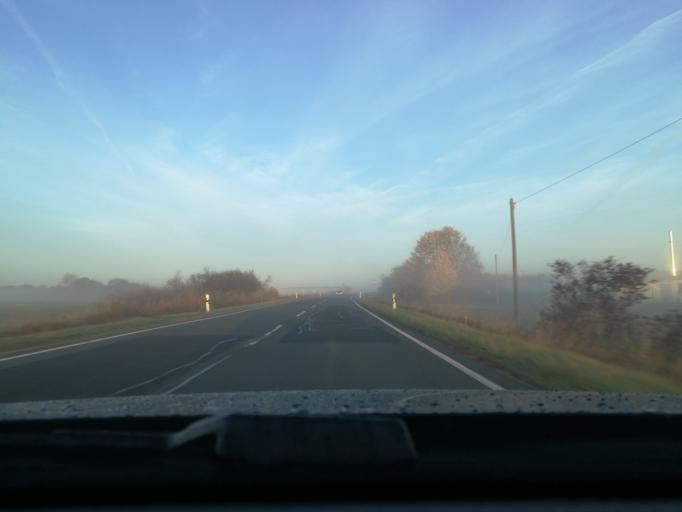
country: DE
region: Bavaria
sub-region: Regierungsbezirk Mittelfranken
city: Obermichelbach
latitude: 49.5359
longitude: 10.9423
